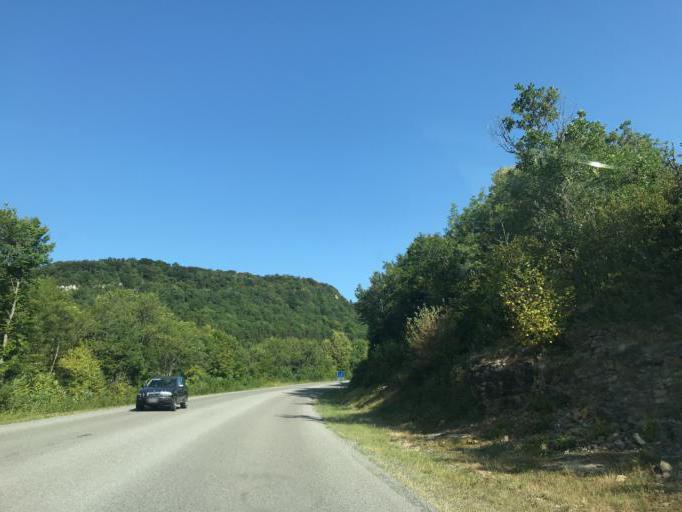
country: FR
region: Franche-Comte
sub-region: Departement du Jura
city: Lavans-les-Saint-Claude
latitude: 46.3843
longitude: 5.7470
